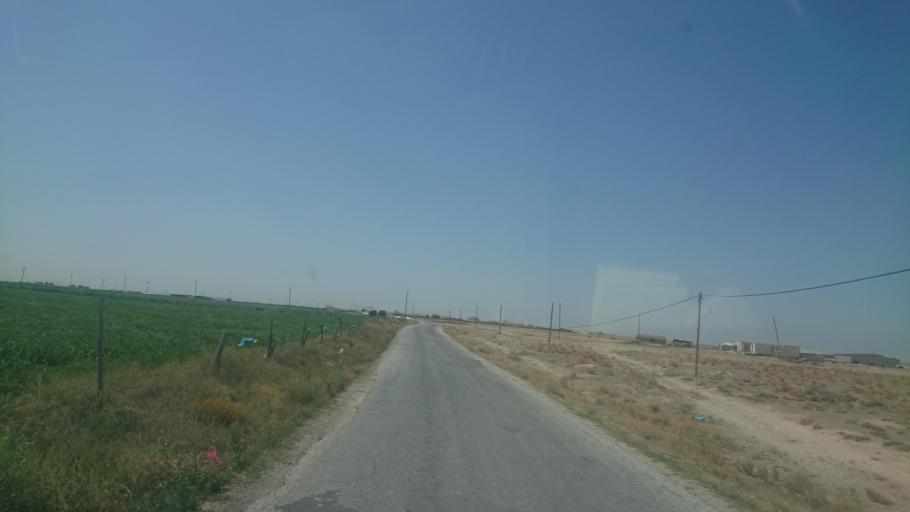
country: TR
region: Aksaray
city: Yesilova
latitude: 38.2949
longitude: 33.7256
